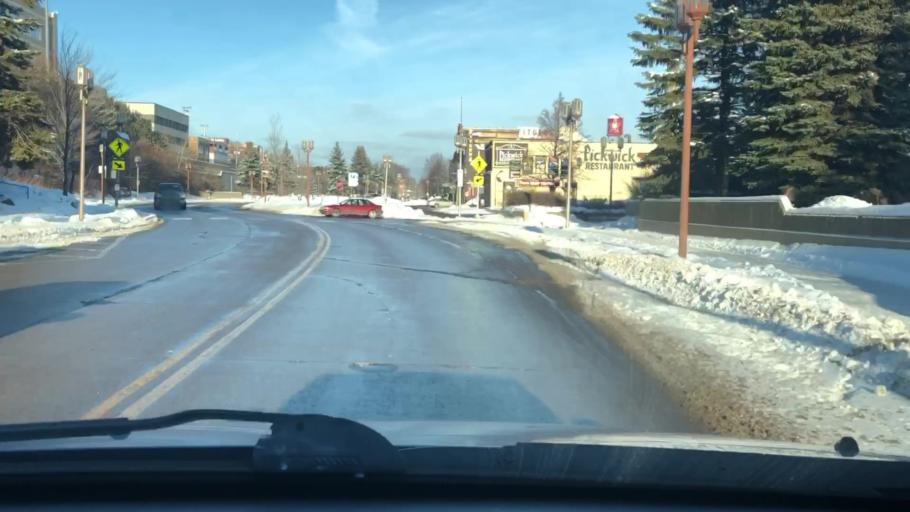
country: US
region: Minnesota
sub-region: Saint Louis County
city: Duluth
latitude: 46.7910
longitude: -92.0929
